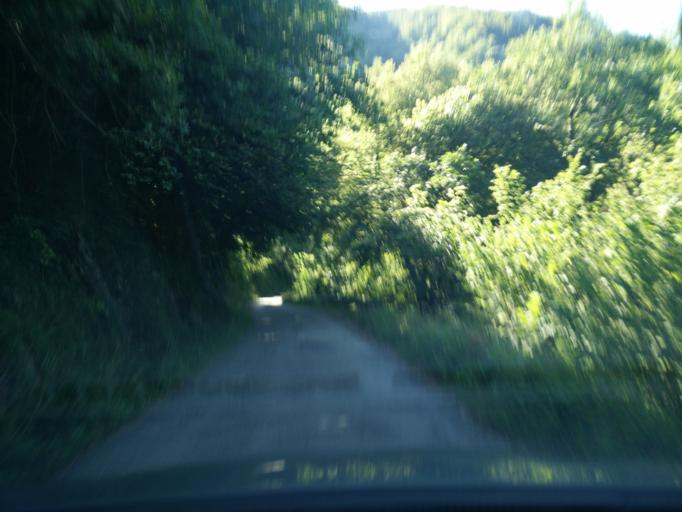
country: ES
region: Asturias
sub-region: Province of Asturias
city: Amieva
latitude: 43.1770
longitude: -5.1721
